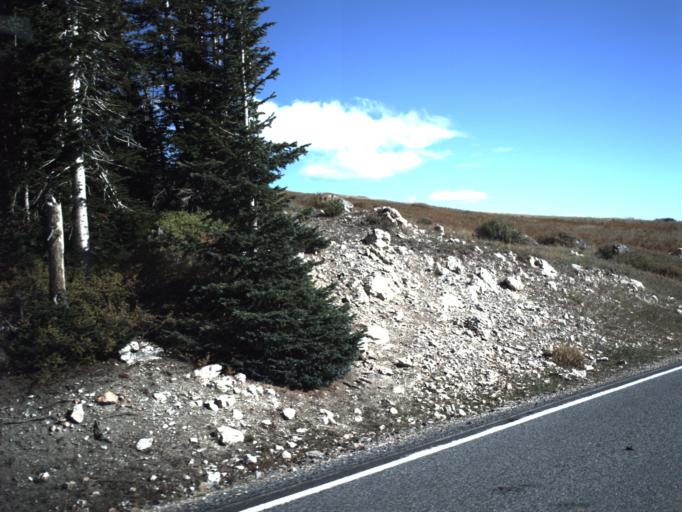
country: US
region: Utah
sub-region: Iron County
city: Parowan
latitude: 37.6750
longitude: -112.8417
